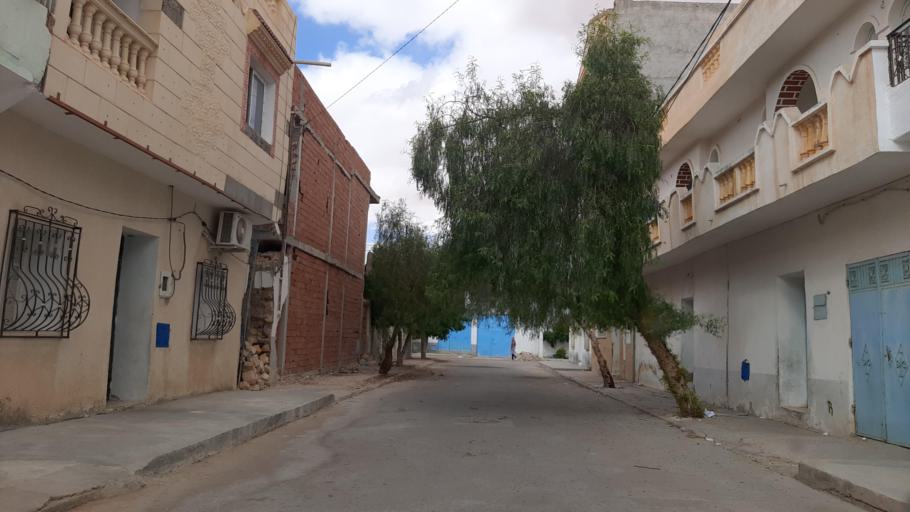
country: TN
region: Tataouine
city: Tataouine
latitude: 32.9347
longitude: 10.4506
